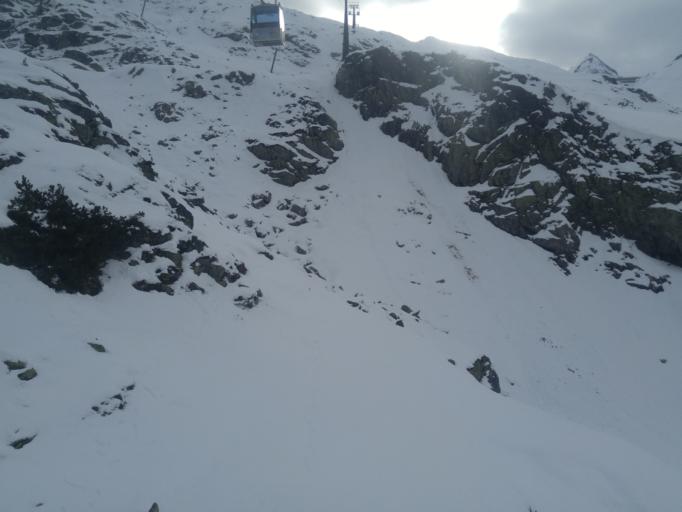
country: AT
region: Salzburg
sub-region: Politischer Bezirk Zell am See
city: Niedernsill
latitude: 47.1428
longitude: 12.6250
